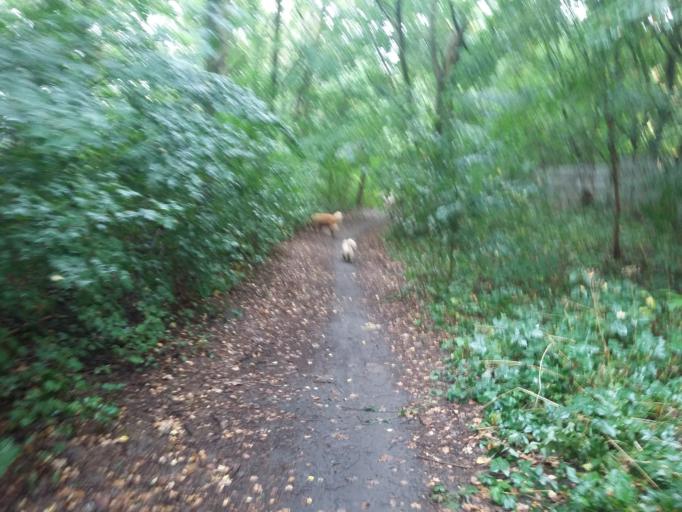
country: PL
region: Lodz Voivodeship
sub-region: Powiat pabianicki
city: Konstantynow Lodzki
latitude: 51.7548
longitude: 19.3907
